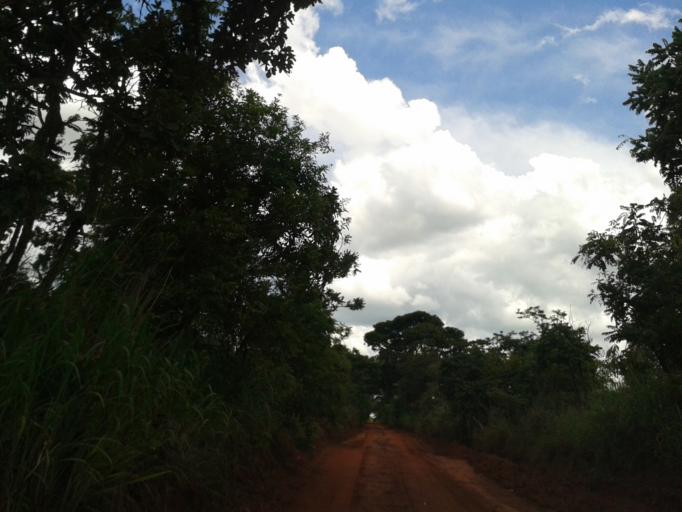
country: BR
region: Minas Gerais
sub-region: Ituiutaba
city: Ituiutaba
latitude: -18.8477
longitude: -49.5099
